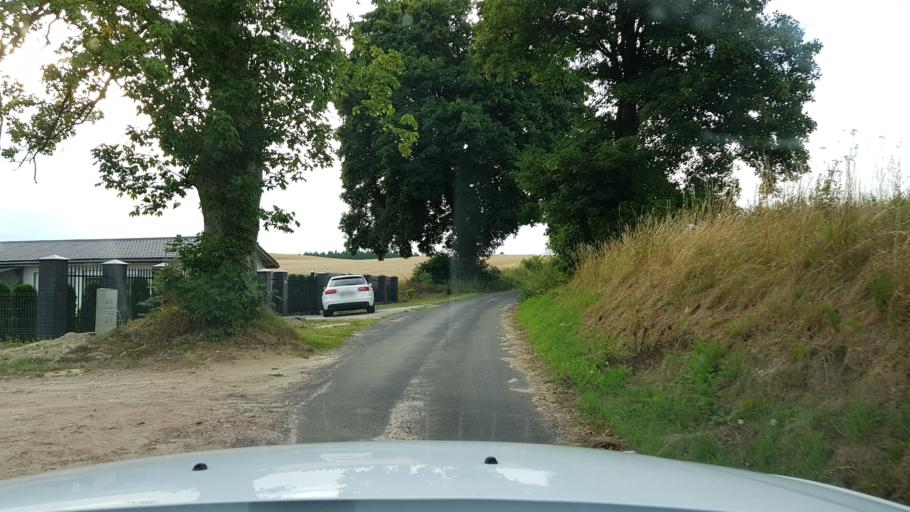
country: PL
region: West Pomeranian Voivodeship
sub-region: Powiat swidwinski
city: Polczyn-Zdroj
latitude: 53.7808
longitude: 16.0892
